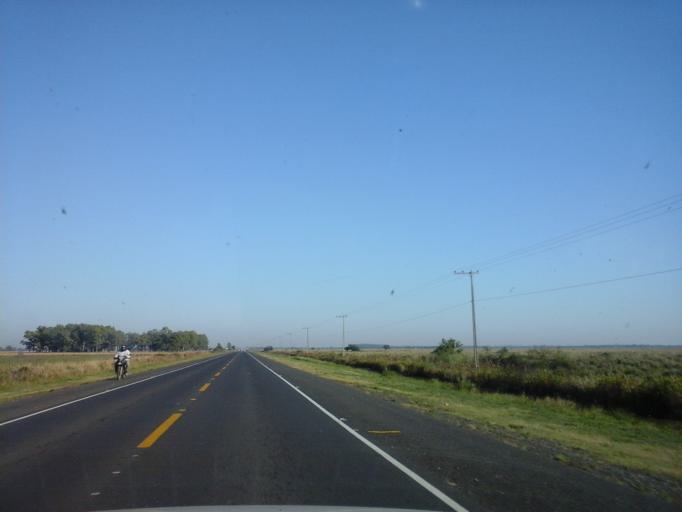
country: PY
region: Neembucu
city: Pilar
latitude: -26.8471
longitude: -58.2454
